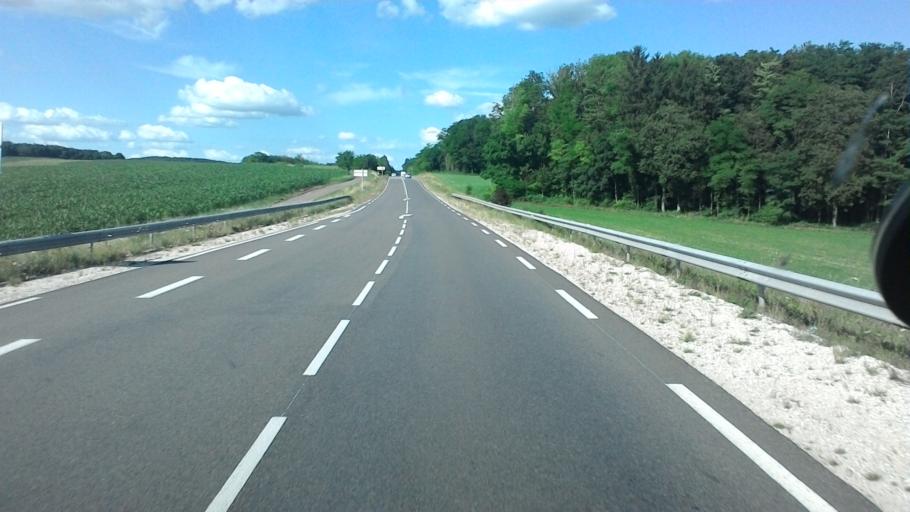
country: FR
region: Franche-Comte
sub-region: Departement de la Haute-Saone
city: Rioz
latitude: 47.5165
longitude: 6.0019
